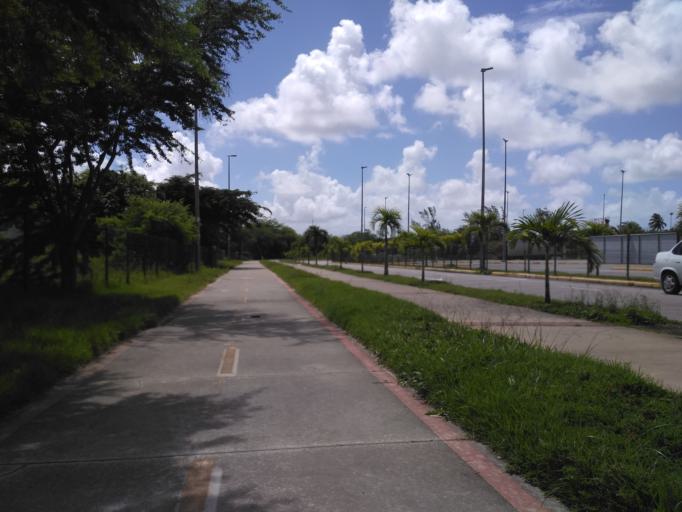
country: BR
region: Pernambuco
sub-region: Recife
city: Recife
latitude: -8.0854
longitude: -34.8968
